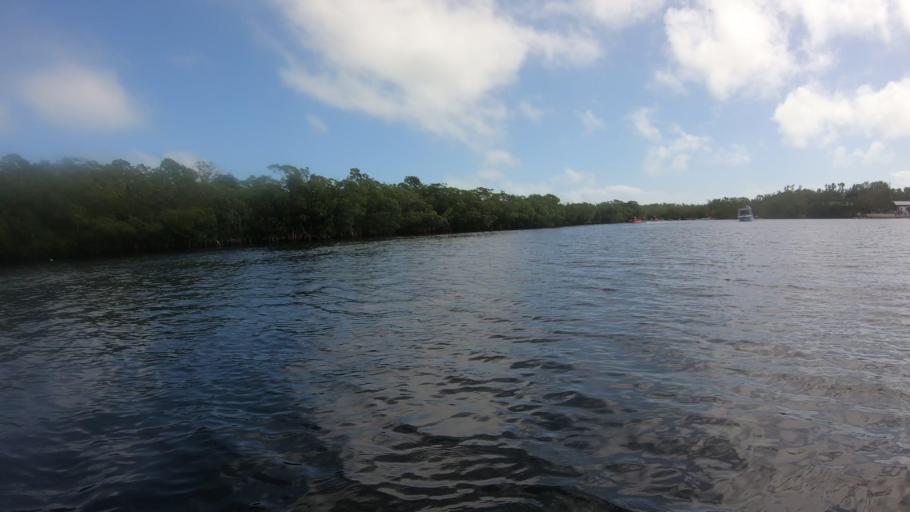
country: US
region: Florida
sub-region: Monroe County
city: Key Largo
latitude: 25.1264
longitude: -80.4020
